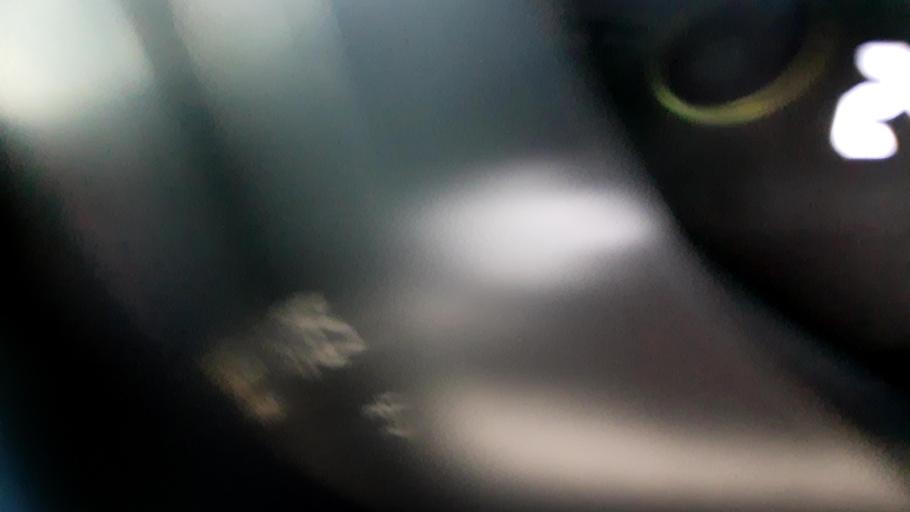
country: RU
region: Nizjnij Novgorod
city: Bor
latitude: 56.3634
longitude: 44.0732
